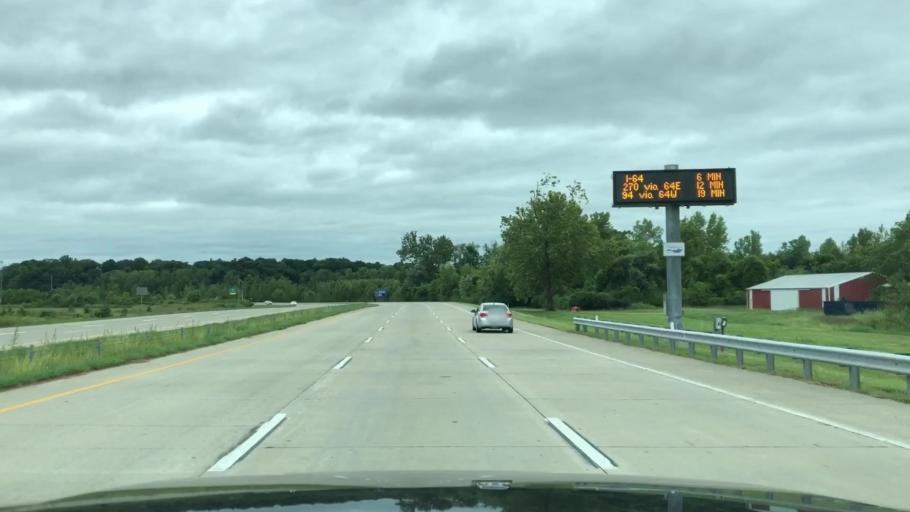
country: US
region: Missouri
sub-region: Saint Louis County
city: Maryland Heights
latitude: 38.7014
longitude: -90.5036
